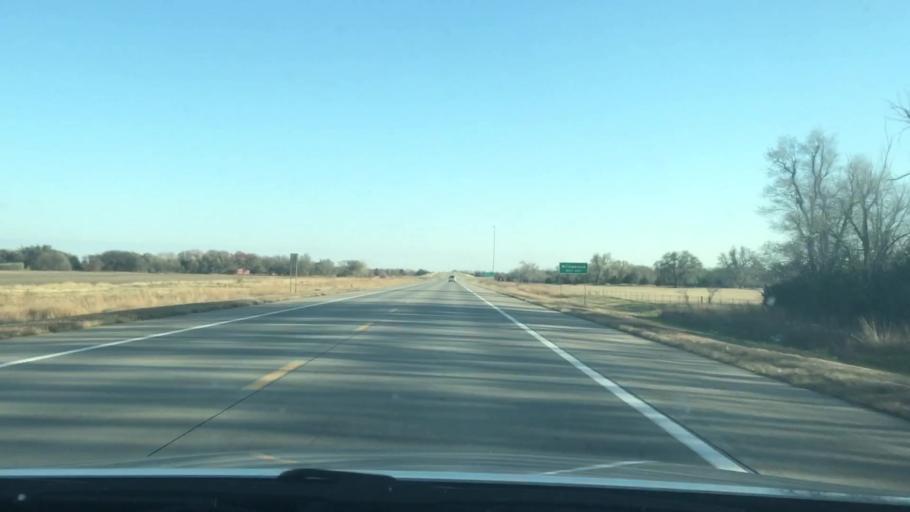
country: US
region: Kansas
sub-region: Reno County
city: Hutchinson
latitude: 38.0976
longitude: -98.0061
